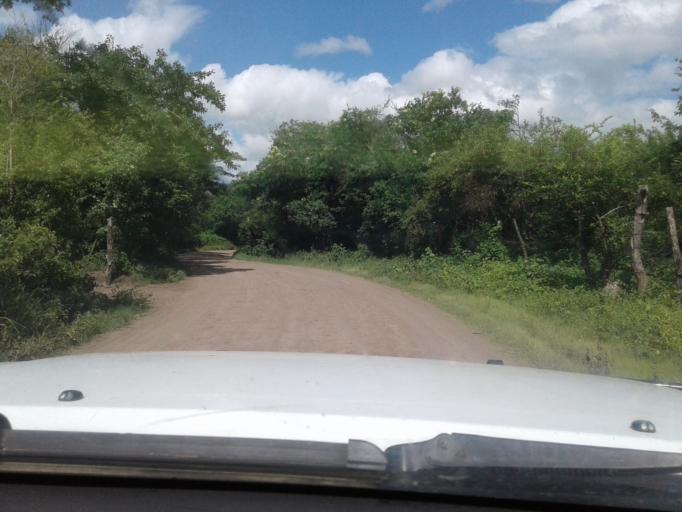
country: NI
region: Matagalpa
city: Ciudad Dario
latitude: 12.8419
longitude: -86.1101
